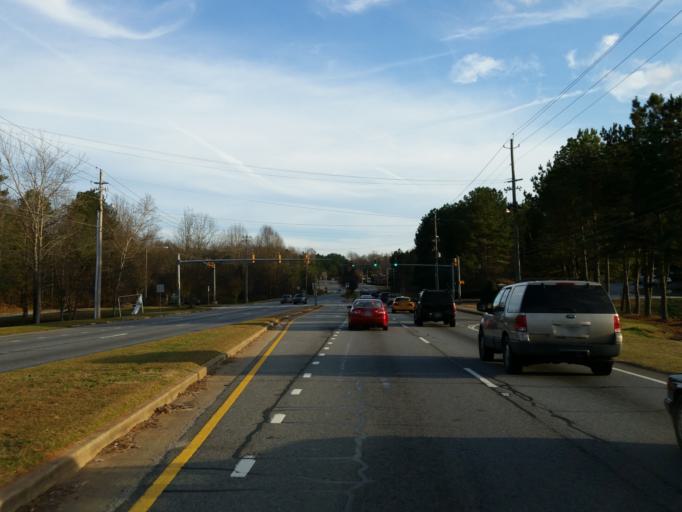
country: US
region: Georgia
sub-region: Cobb County
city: Austell
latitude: 33.8583
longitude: -84.6173
